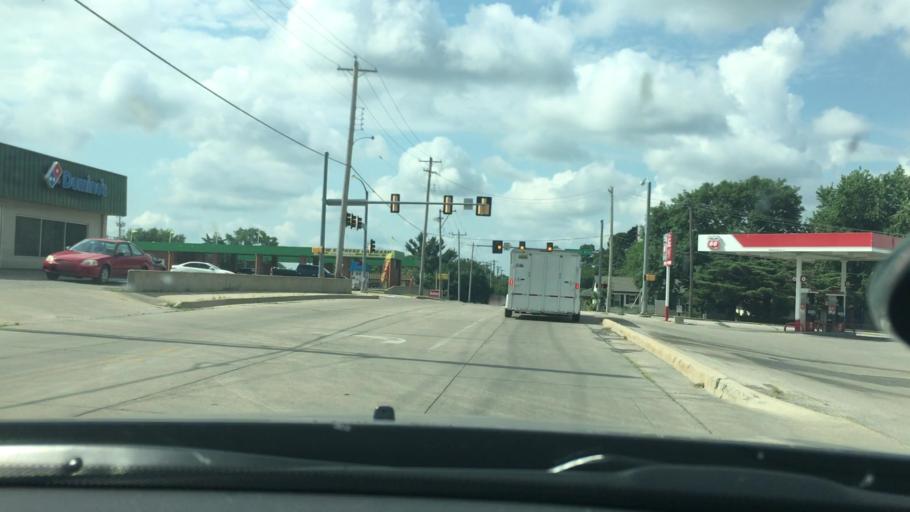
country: US
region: Oklahoma
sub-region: Bryan County
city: Durant
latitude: 34.0056
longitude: -96.3905
